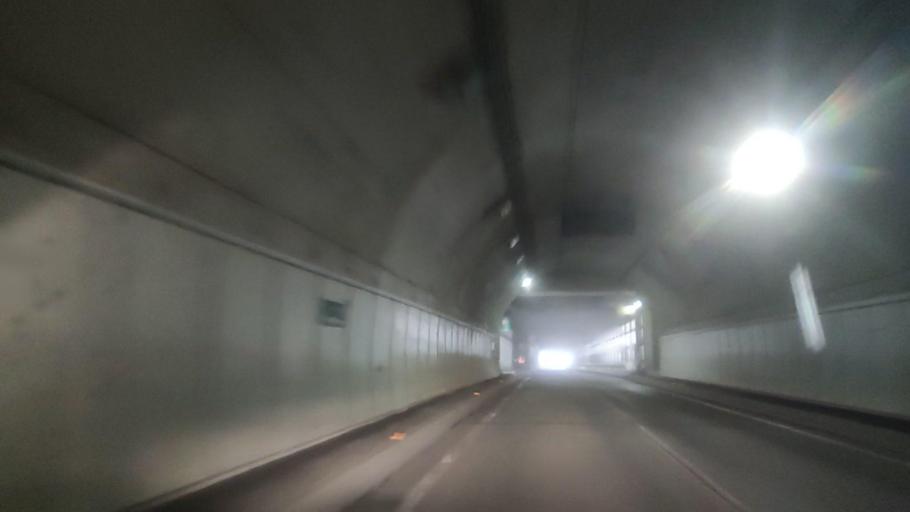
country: JP
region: Hokkaido
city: Date
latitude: 42.5517
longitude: 141.0809
